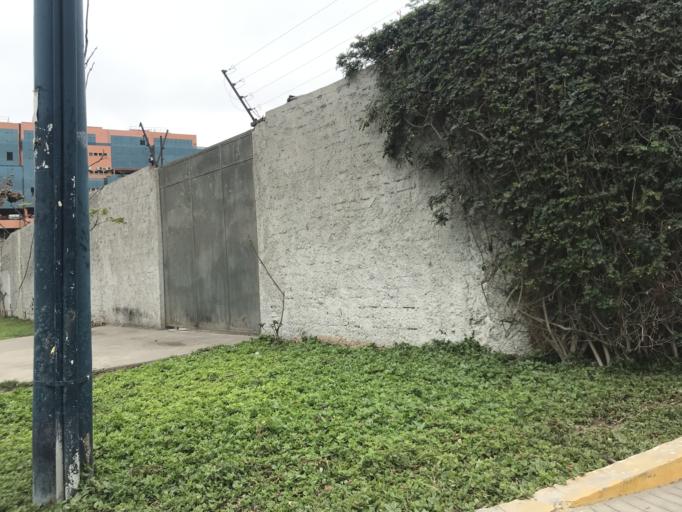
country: PE
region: Lima
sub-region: Lima
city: San Isidro
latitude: -12.0963
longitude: -77.0339
